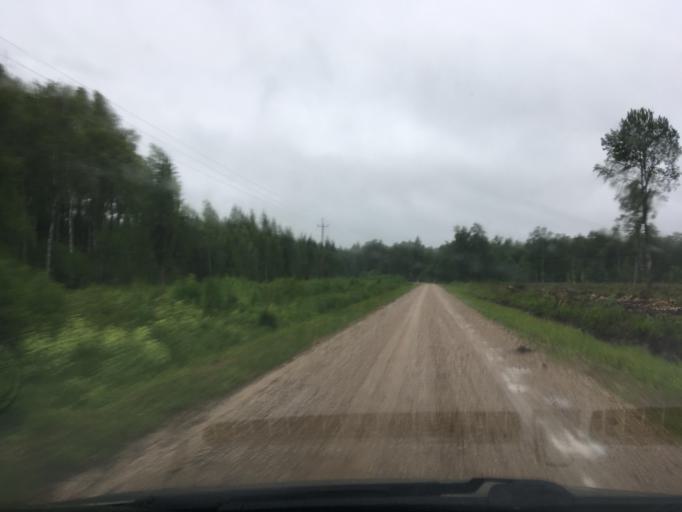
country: EE
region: Laeaene
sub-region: Lihula vald
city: Lihula
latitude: 58.6109
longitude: 23.8270
